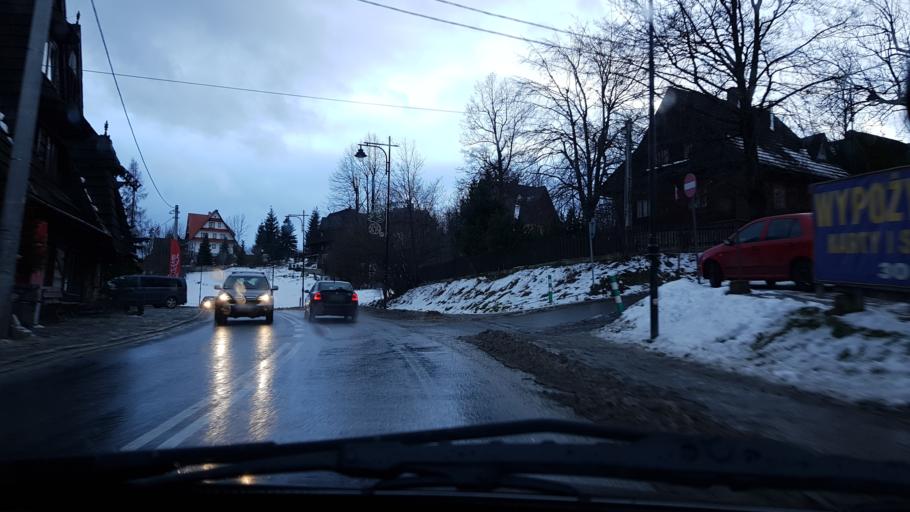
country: PL
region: Lesser Poland Voivodeship
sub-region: Powiat tatrzanski
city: Bukowina Tatrzanska
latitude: 49.3326
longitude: 20.0966
